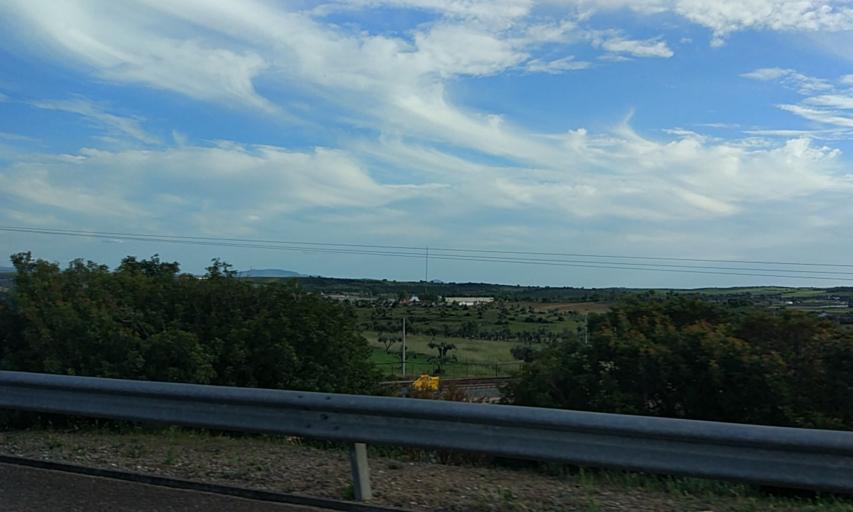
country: PT
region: Portalegre
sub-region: Elvas
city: Elvas
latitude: 38.8989
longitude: -7.1300
